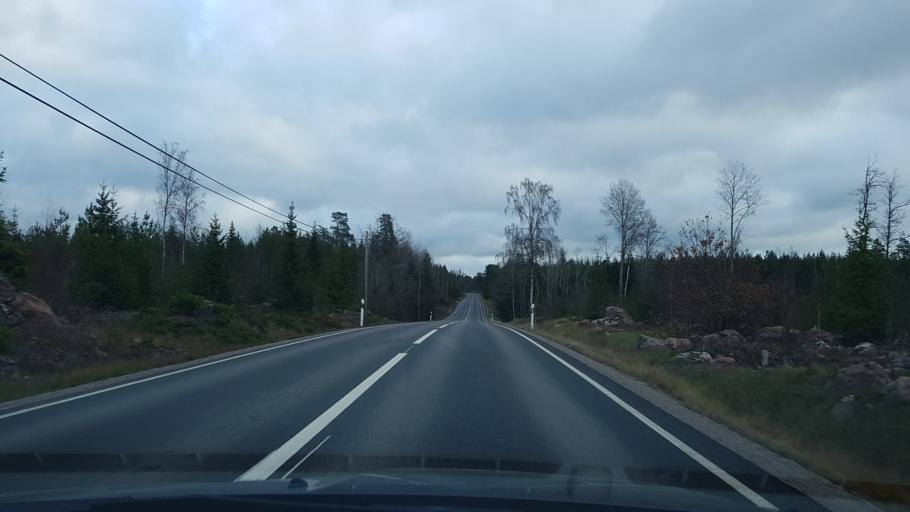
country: SE
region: Stockholm
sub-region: Norrtalje Kommun
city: Skanninge
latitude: 60.0175
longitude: 18.3754
